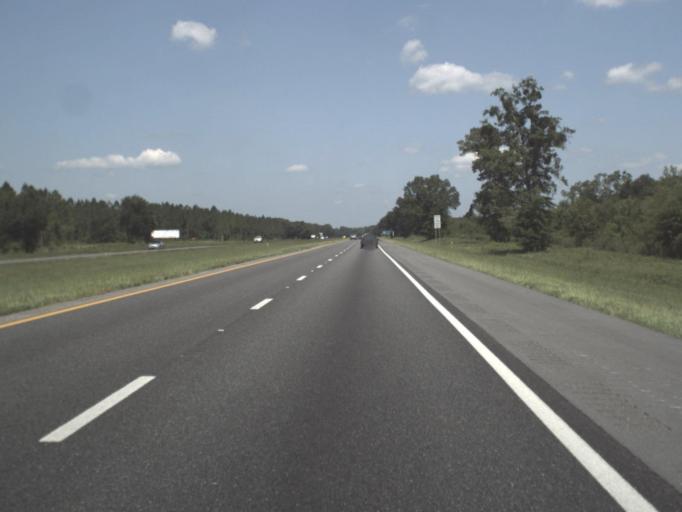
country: US
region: Florida
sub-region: Madison County
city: Madison
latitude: 30.3825
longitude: -83.3078
